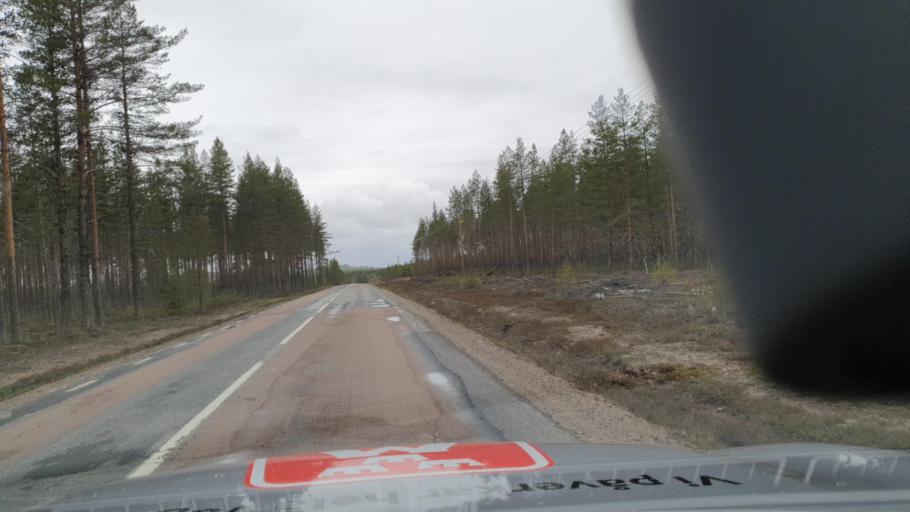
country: SE
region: Vaesternorrland
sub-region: Solleftea Kommun
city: Solleftea
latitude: 63.6182
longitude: 17.4808
